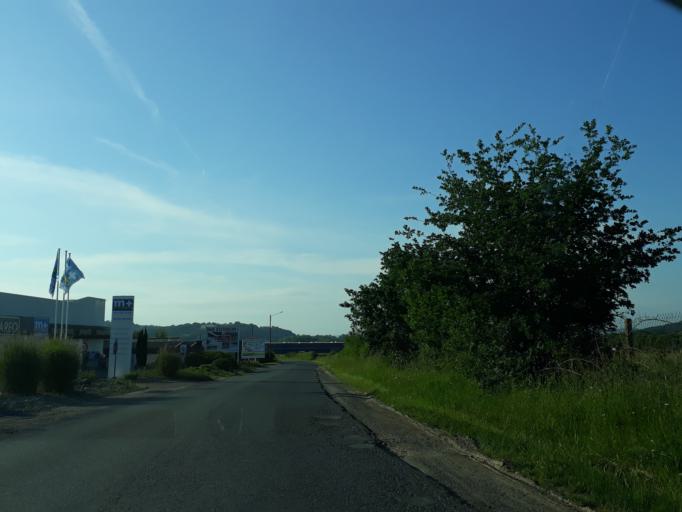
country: FR
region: Limousin
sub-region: Departement de la Correze
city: Saint-Pantaleon-de-Larche
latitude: 45.1487
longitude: 1.4698
